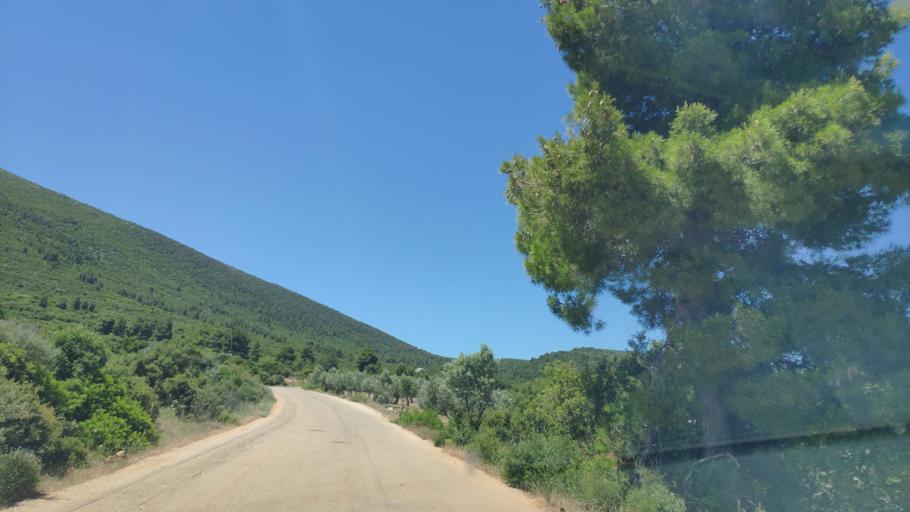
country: GR
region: Central Greece
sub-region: Nomos Voiotias
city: Kaparellion
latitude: 38.2106
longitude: 23.1866
